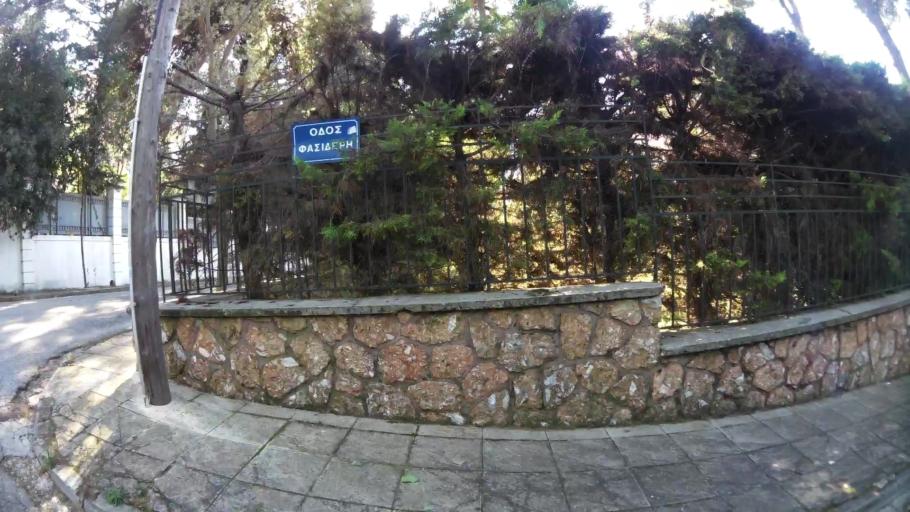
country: GR
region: Attica
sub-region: Nomarchia Athinas
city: Ekali
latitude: 38.1113
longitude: 23.8359
